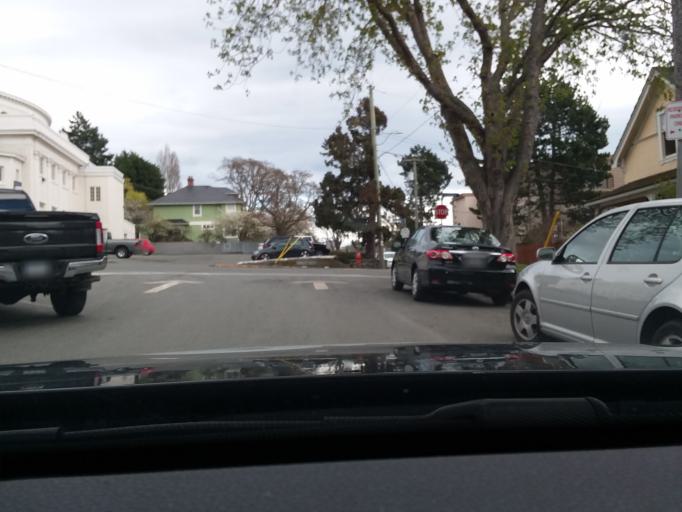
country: CA
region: British Columbia
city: Victoria
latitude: 48.4266
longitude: -123.3509
